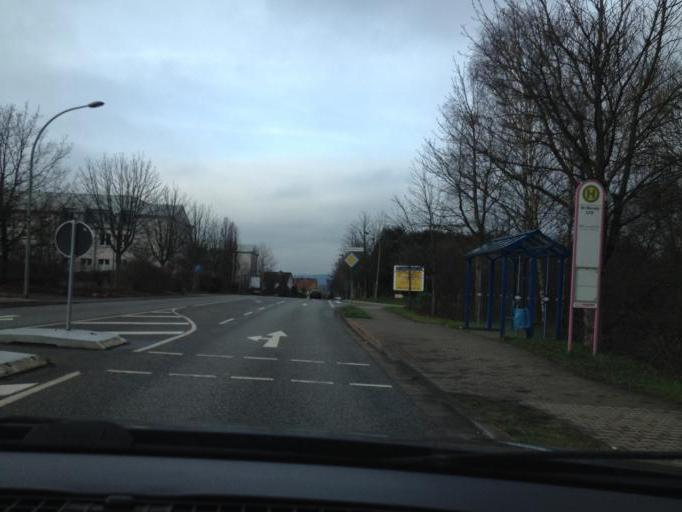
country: DE
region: Saarland
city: Sankt Wendel
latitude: 49.4587
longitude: 7.1767
